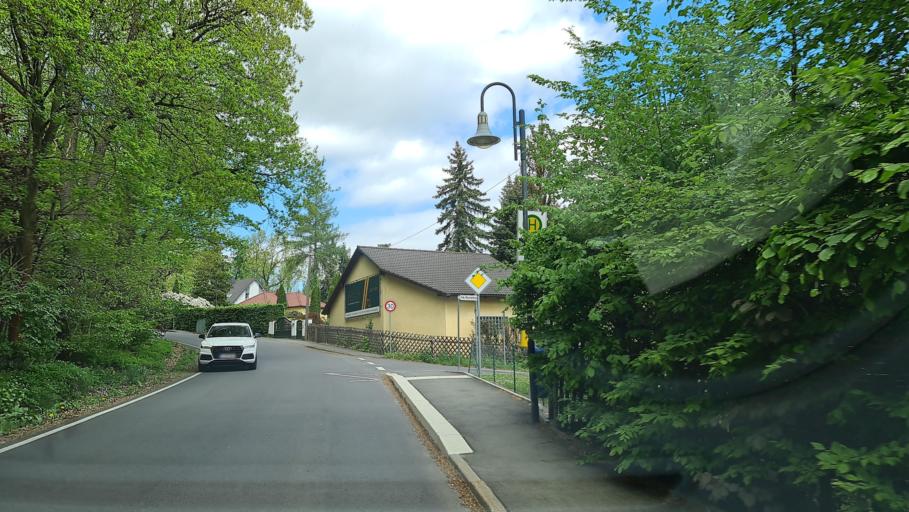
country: DE
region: Saxony
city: Hilbersdorf
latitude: 50.8466
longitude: 12.9859
